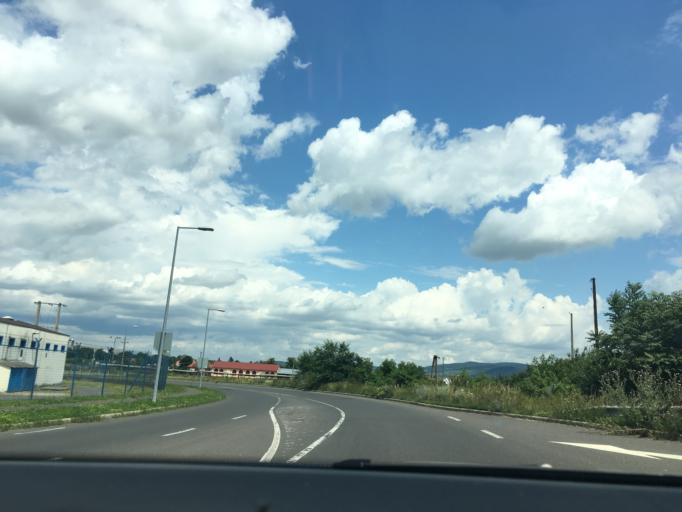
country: HU
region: Borsod-Abauj-Zemplen
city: Satoraljaujhely
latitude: 48.3913
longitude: 21.6643
